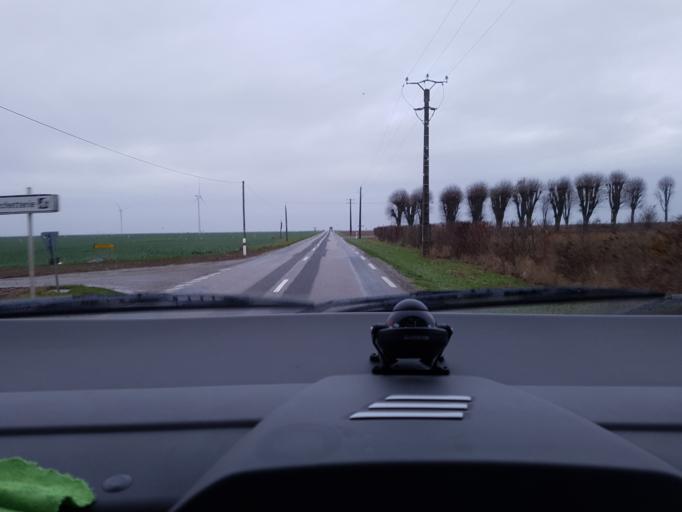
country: FR
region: Haute-Normandie
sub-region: Departement de l'Eure
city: Beaumont-le-Roger
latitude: 49.0974
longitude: 0.8131
